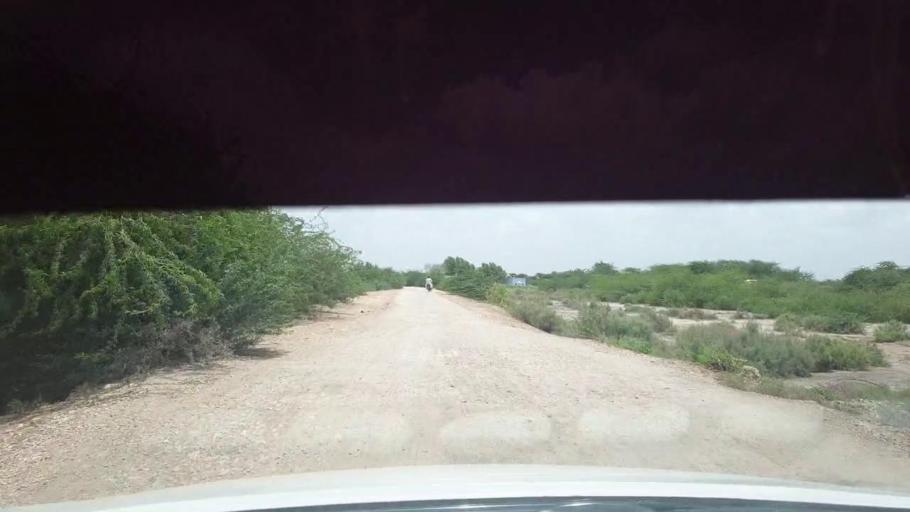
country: PK
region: Sindh
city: Kadhan
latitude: 24.4638
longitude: 69.0281
